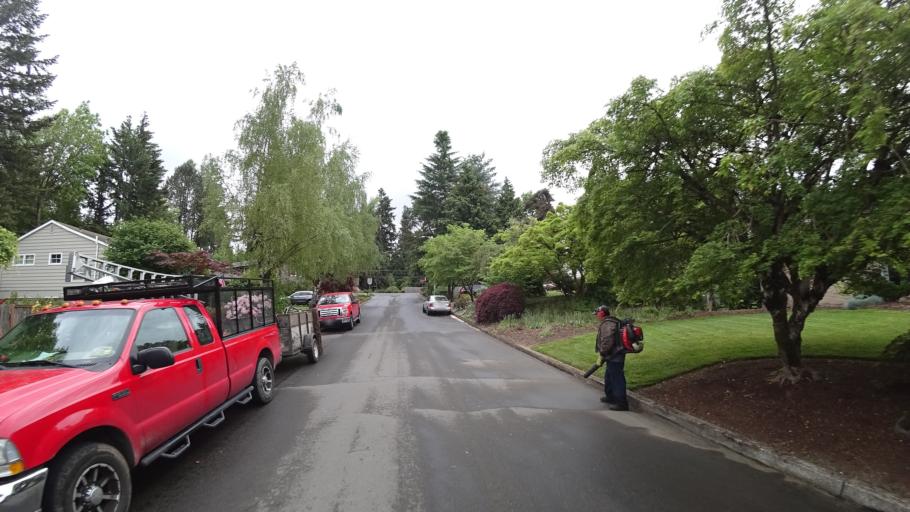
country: US
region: Oregon
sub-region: Washington County
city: Garden Home-Whitford
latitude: 45.4665
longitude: -122.7668
